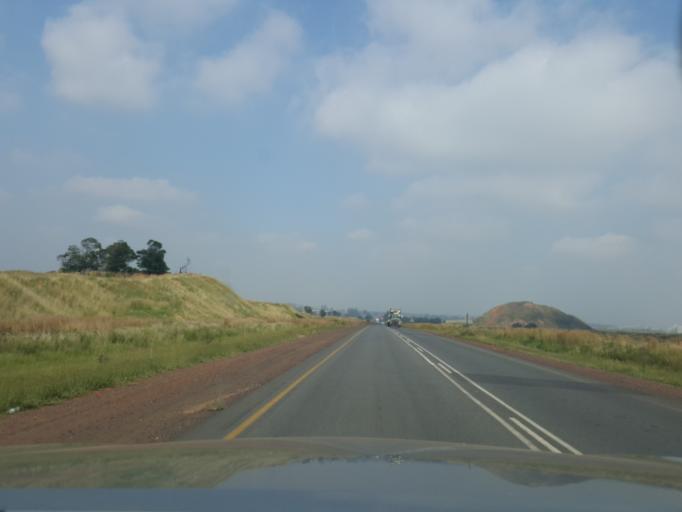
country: ZA
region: Mpumalanga
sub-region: Nkangala District Municipality
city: Witbank
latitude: -26.0145
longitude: 29.3879
